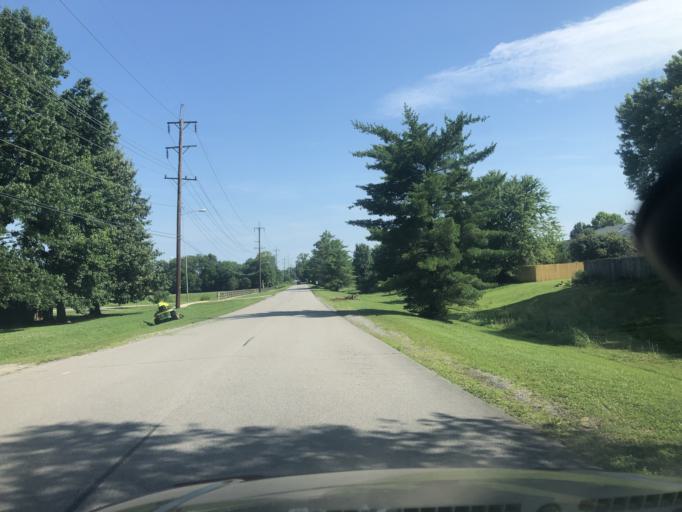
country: US
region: Tennessee
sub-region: Davidson County
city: Lakewood
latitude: 36.2357
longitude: -86.6999
